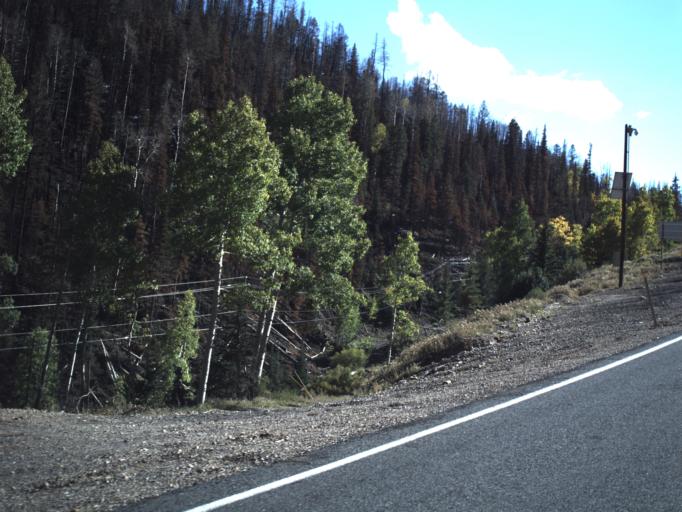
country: US
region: Utah
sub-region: Iron County
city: Parowan
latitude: 37.7210
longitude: -112.8443
